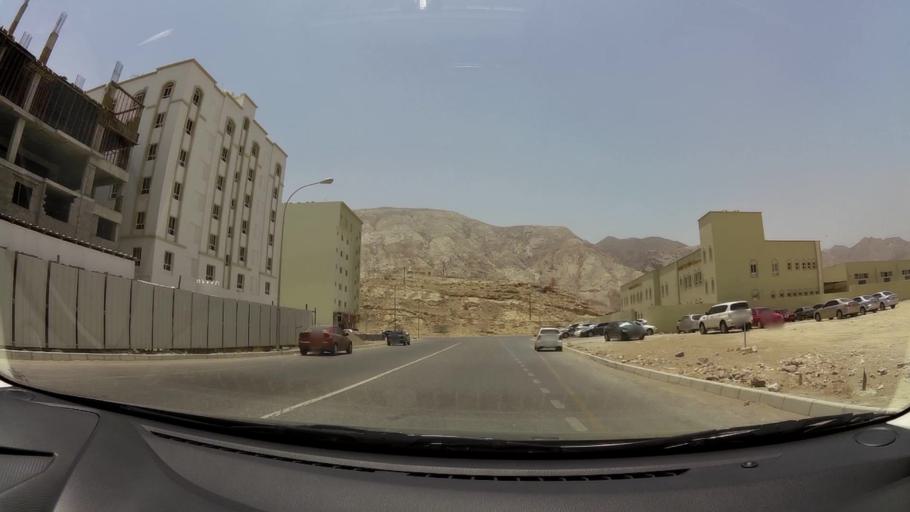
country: OM
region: Muhafazat Masqat
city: Bawshar
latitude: 23.5576
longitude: 58.4101
